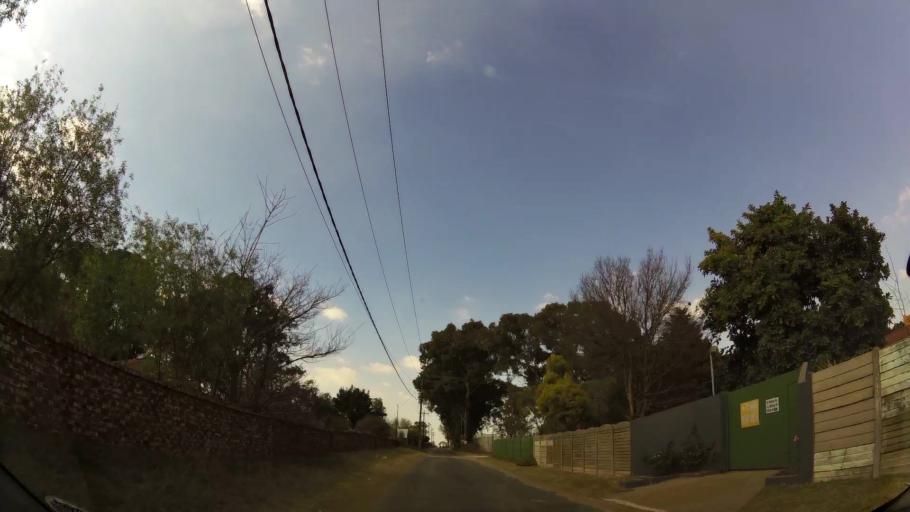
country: ZA
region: Gauteng
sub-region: Ekurhuleni Metropolitan Municipality
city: Benoni
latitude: -26.1052
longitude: 28.3662
